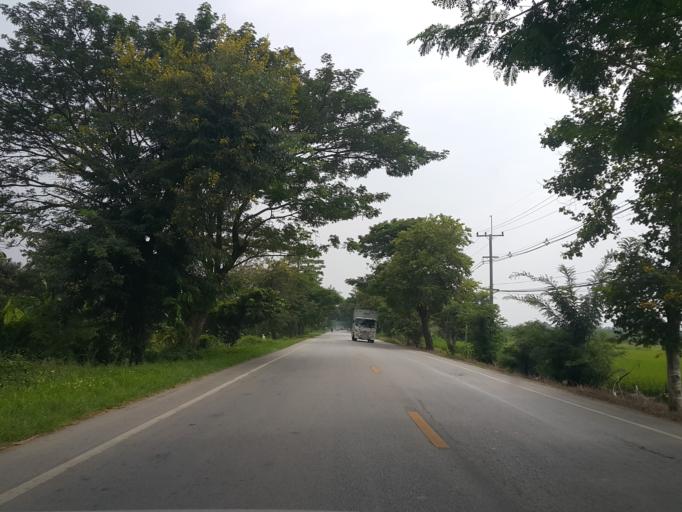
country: TH
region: Chiang Mai
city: Mae Taeng
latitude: 19.0225
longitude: 98.9689
